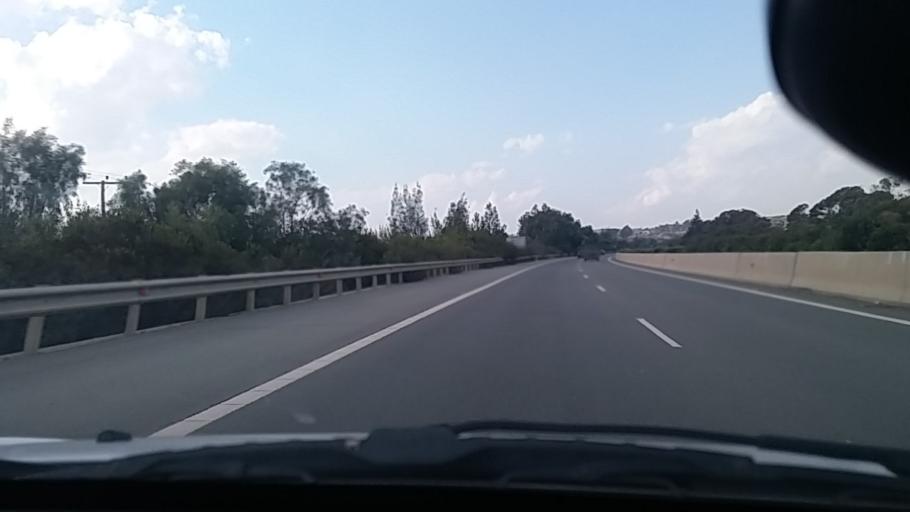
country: CY
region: Lefkosia
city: Kokkinotrimithia
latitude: 35.1458
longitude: 33.2508
